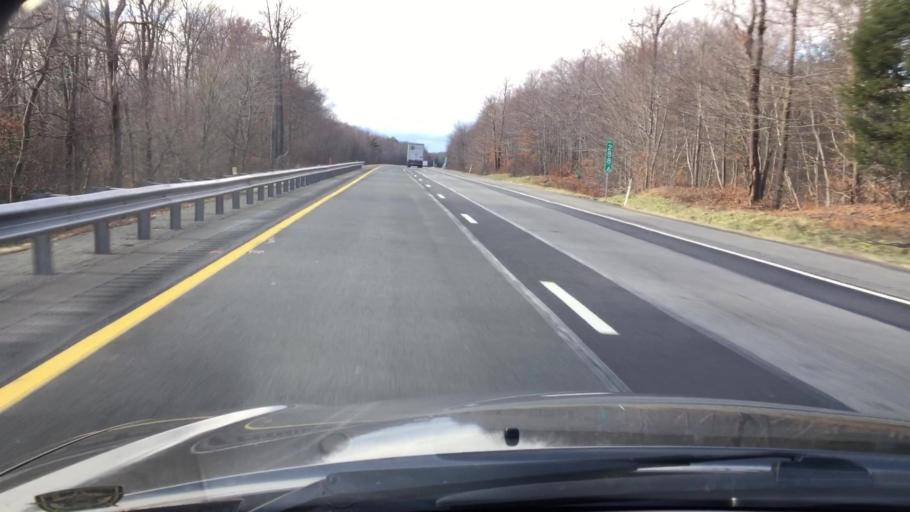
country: US
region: Pennsylvania
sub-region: Monroe County
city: Pocono Pines
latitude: 41.0740
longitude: -75.4803
